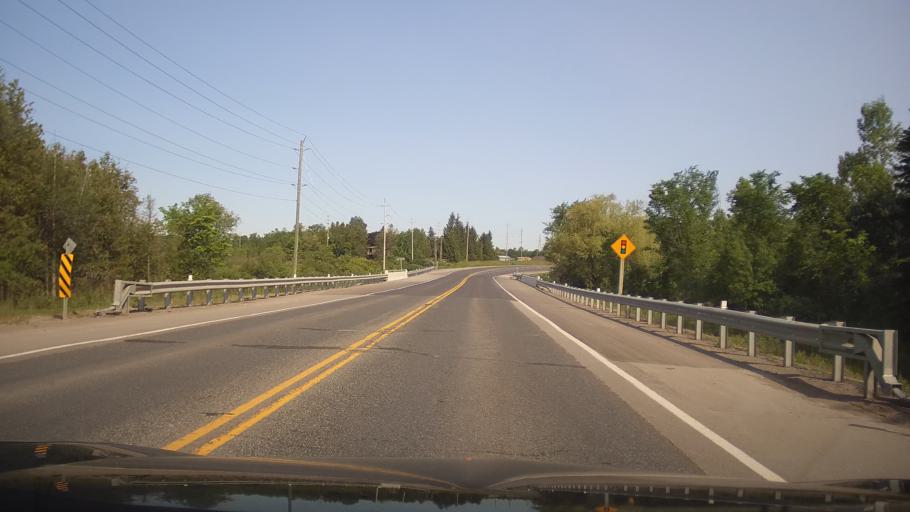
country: CA
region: Ontario
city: Peterborough
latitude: 44.2764
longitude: -78.4160
